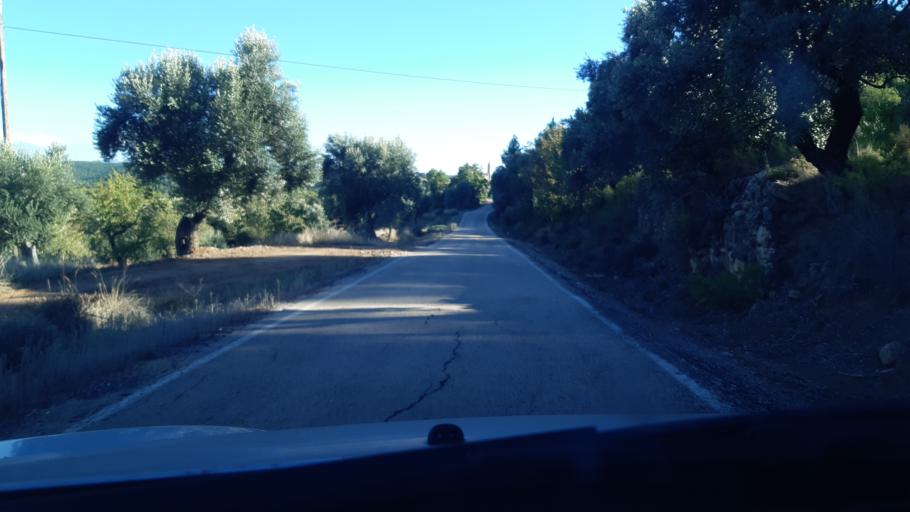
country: ES
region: Aragon
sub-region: Provincia de Teruel
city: Fornoles
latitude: 40.9066
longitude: -0.0126
